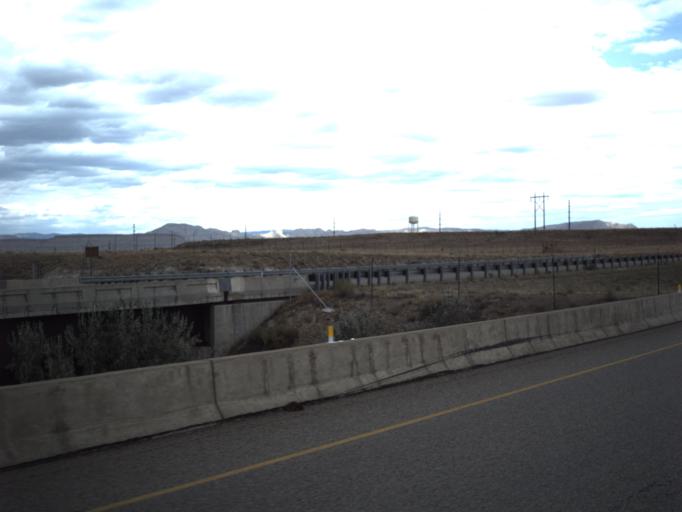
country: US
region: Utah
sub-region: Carbon County
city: East Carbon City
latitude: 38.9742
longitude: -110.1494
